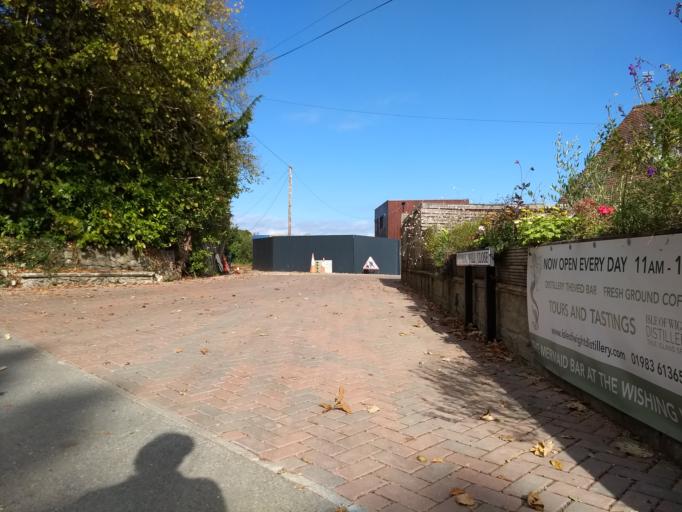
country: GB
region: England
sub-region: Isle of Wight
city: Seaview
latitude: 50.7167
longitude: -1.1245
